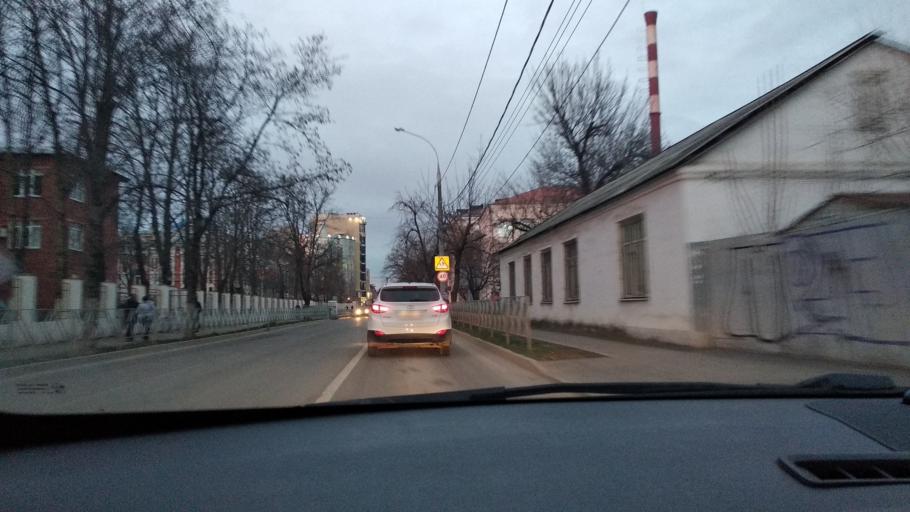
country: RU
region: Krasnodarskiy
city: Krasnodar
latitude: 45.0431
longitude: 38.9745
